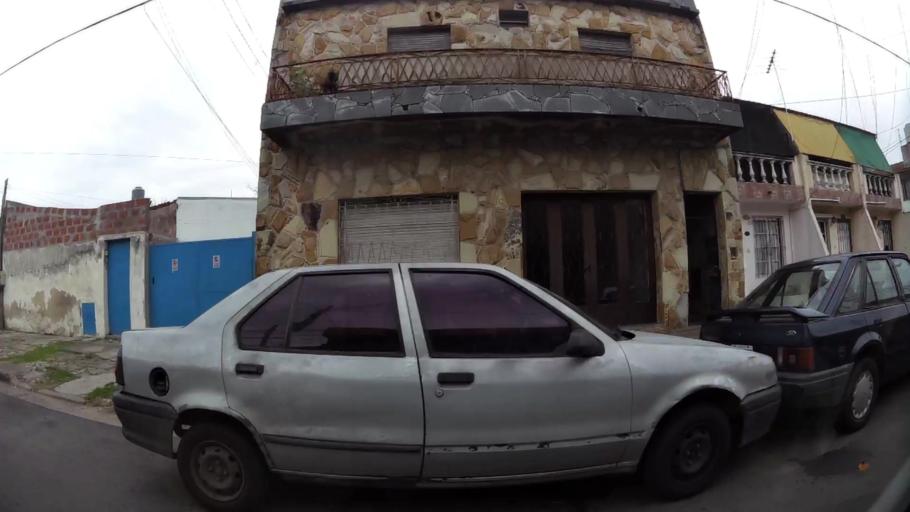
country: AR
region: Buenos Aires F.D.
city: Villa Lugano
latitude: -34.6667
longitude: -58.5145
